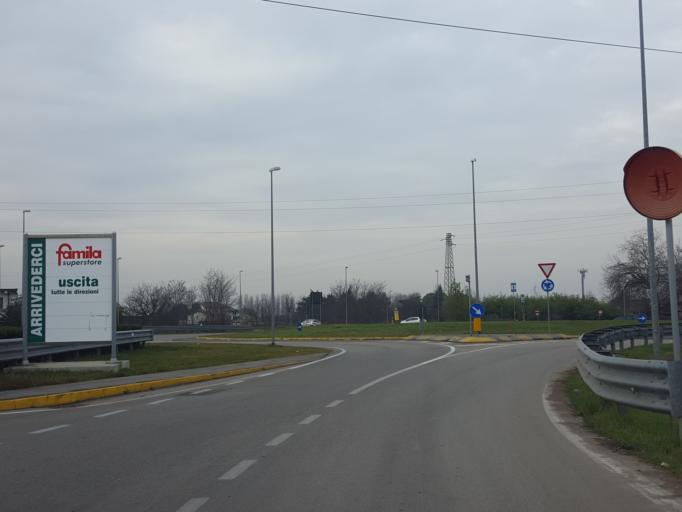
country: IT
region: Veneto
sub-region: Provincia di Verona
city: San Bonifacio
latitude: 45.3865
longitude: 11.2825
